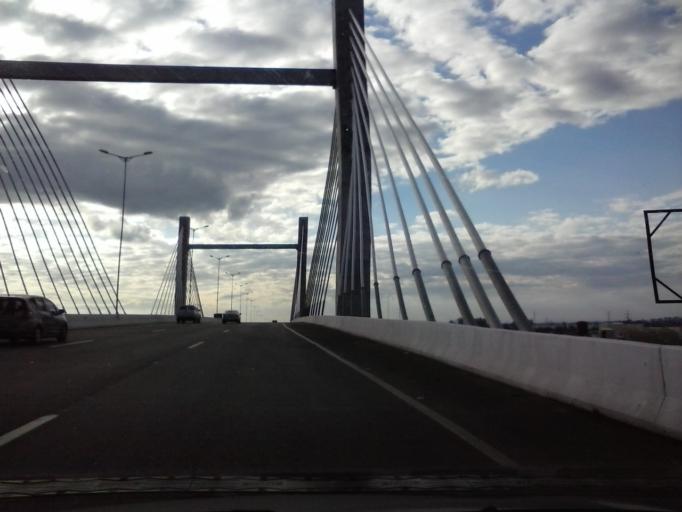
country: BR
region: Rio Grande do Sul
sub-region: Canoas
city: Canoas
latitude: -29.9726
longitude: -51.1992
